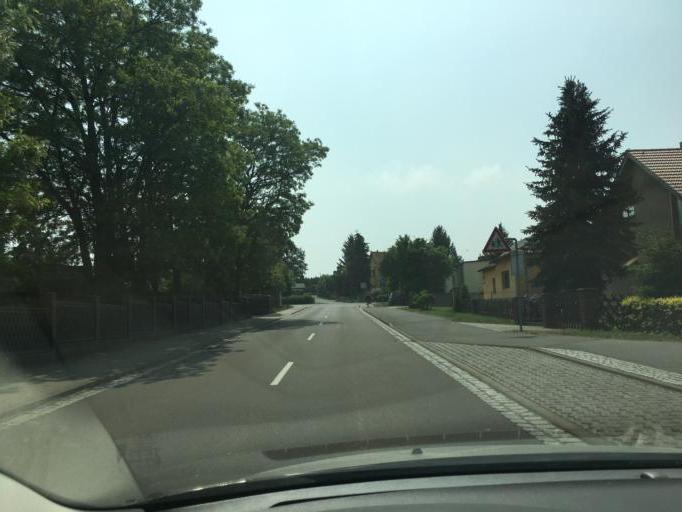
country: DE
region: Saxony
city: Grossposna
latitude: 51.2750
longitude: 12.5047
